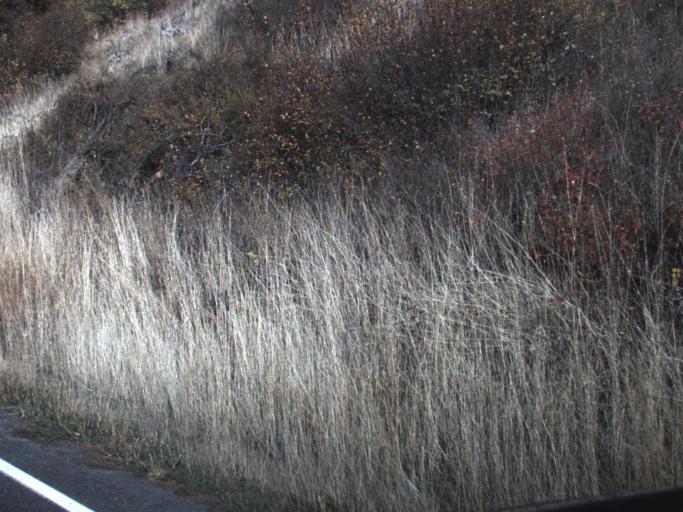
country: US
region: Washington
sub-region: Lincoln County
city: Davenport
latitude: 48.1087
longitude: -118.2040
